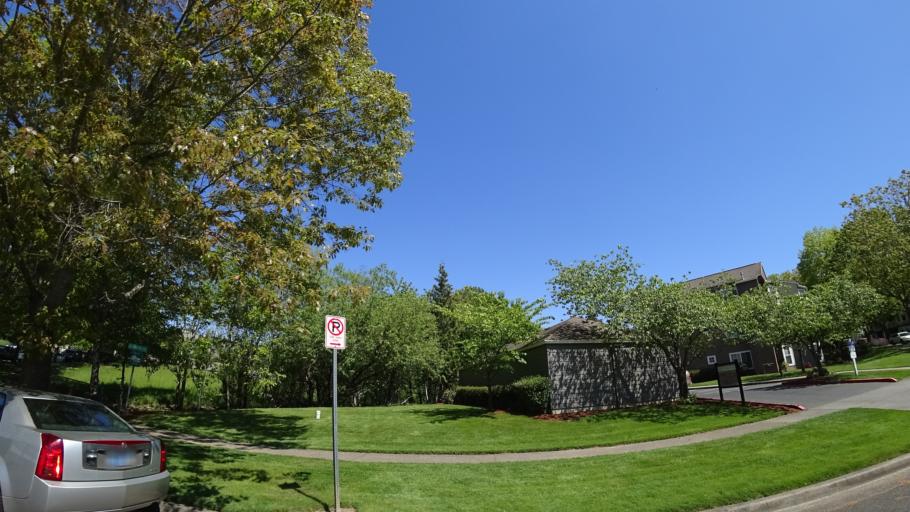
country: US
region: Oregon
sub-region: Washington County
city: Raleigh Hills
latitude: 45.4848
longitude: -122.7648
